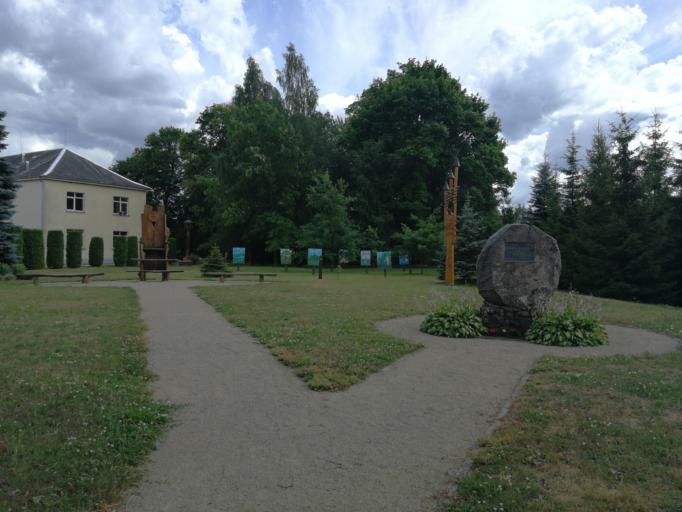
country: LT
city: Vilkija
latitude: 55.0832
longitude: 23.4176
